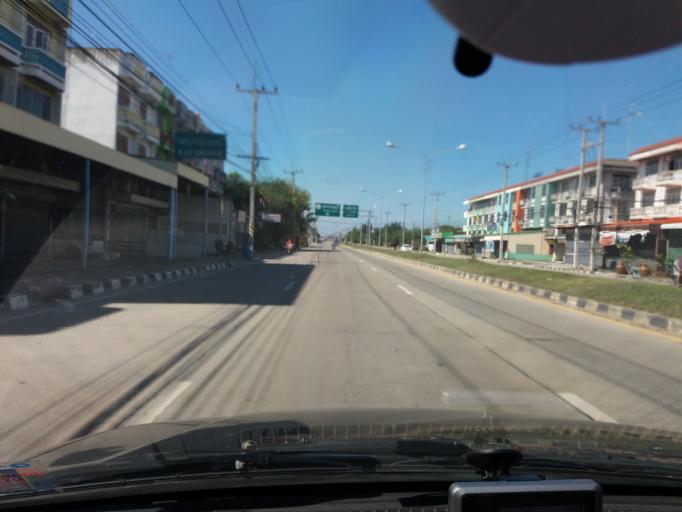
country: TH
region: Suphan Buri
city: Suphan Buri
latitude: 14.4618
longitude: 100.1486
